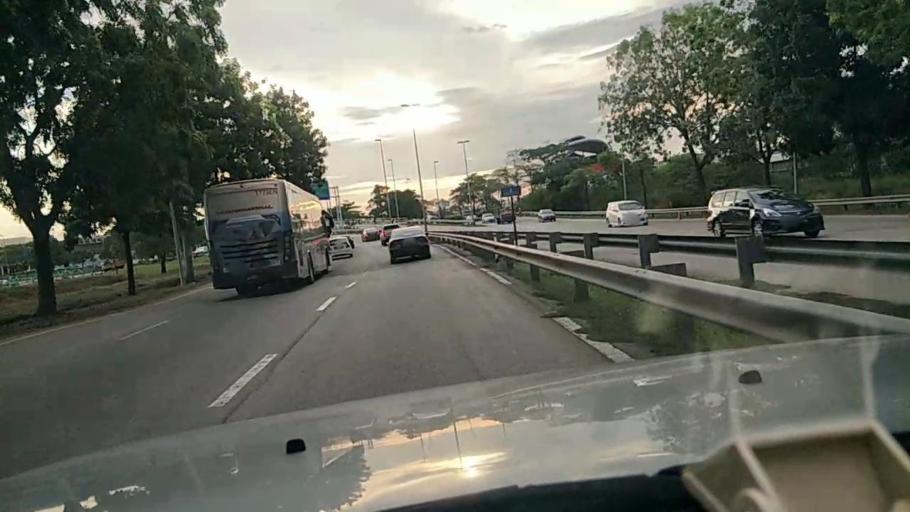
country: MY
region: Selangor
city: Klang
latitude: 3.1093
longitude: 101.4450
